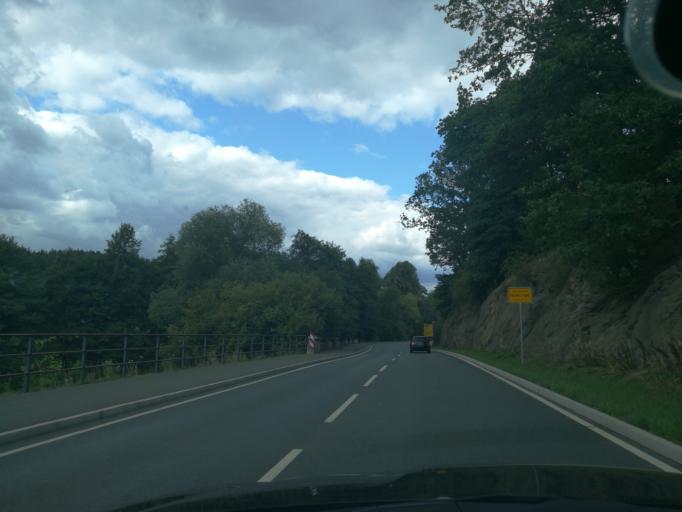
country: DE
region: Saxony
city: Oelsnitz
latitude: 50.3995
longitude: 12.1863
